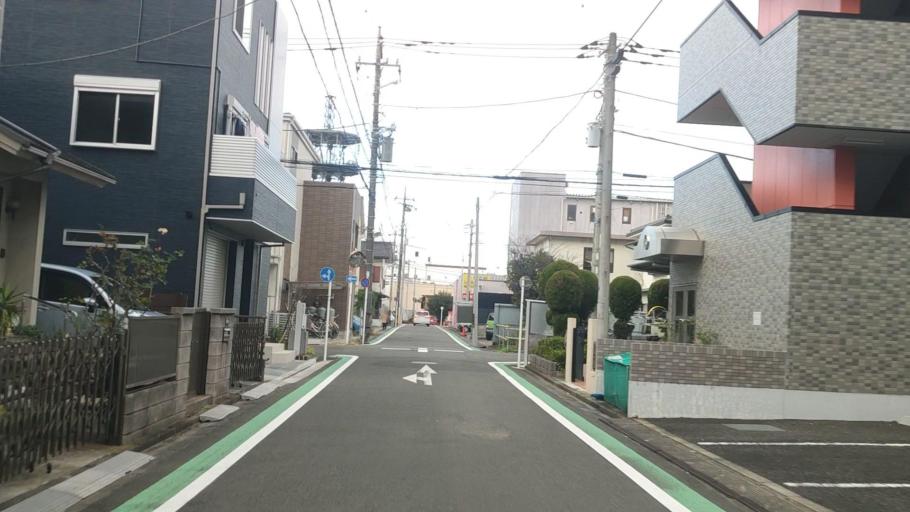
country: JP
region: Kanagawa
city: Minami-rinkan
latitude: 35.4735
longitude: 139.4617
